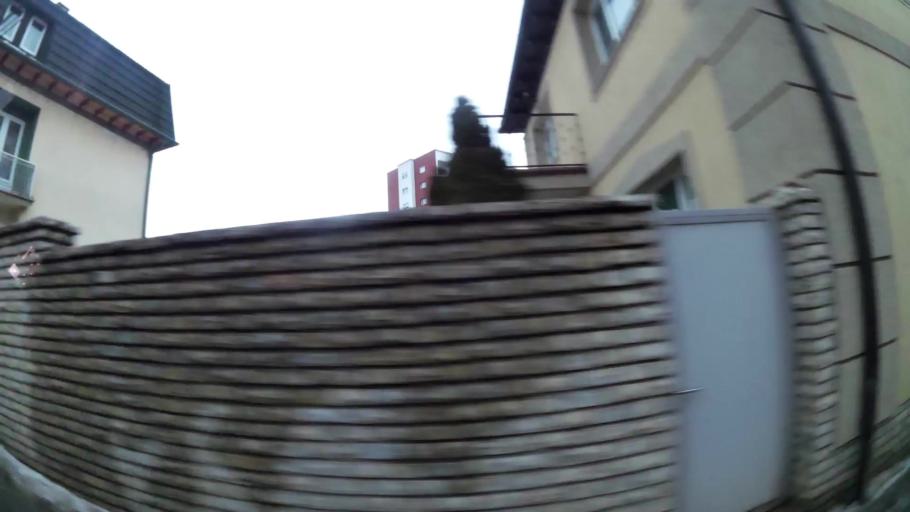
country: XK
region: Pristina
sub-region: Komuna e Prishtines
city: Pristina
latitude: 42.6582
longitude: 21.1722
